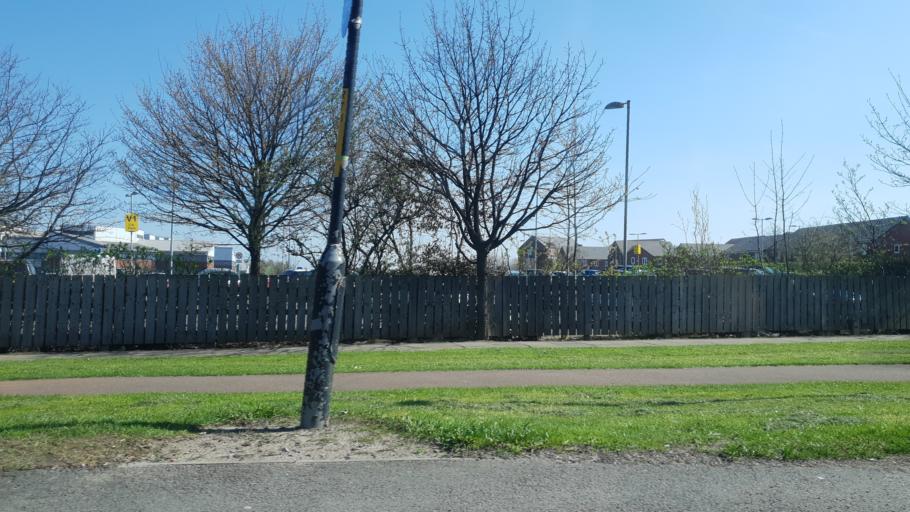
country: GB
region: England
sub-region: Middlesbrough
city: Middlesbrough
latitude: 54.5491
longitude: -1.2171
